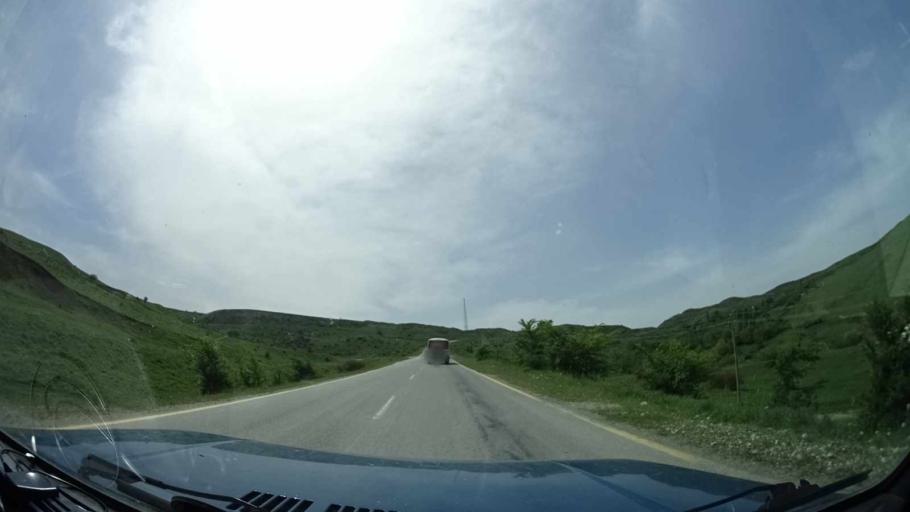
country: AZ
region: Xizi
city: Khyzy
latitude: 40.9048
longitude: 49.1188
